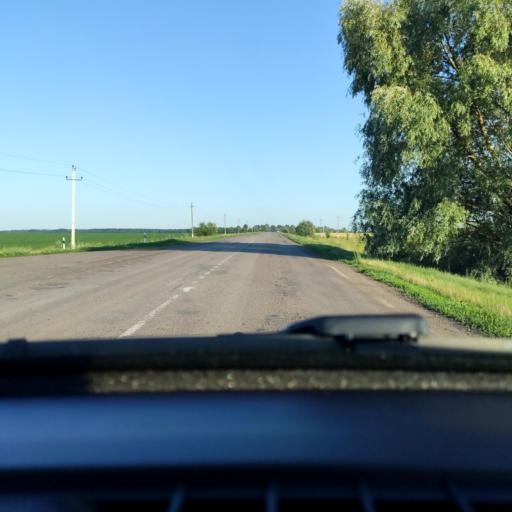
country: RU
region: Voronezj
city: Kashirskoye
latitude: 51.4874
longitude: 39.8529
